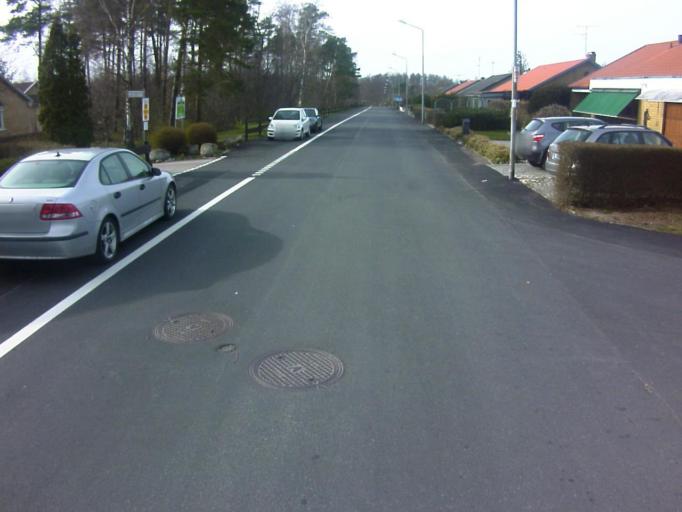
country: SE
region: Skane
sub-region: Kavlinge Kommun
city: Kaevlinge
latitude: 55.7765
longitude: 13.0835
